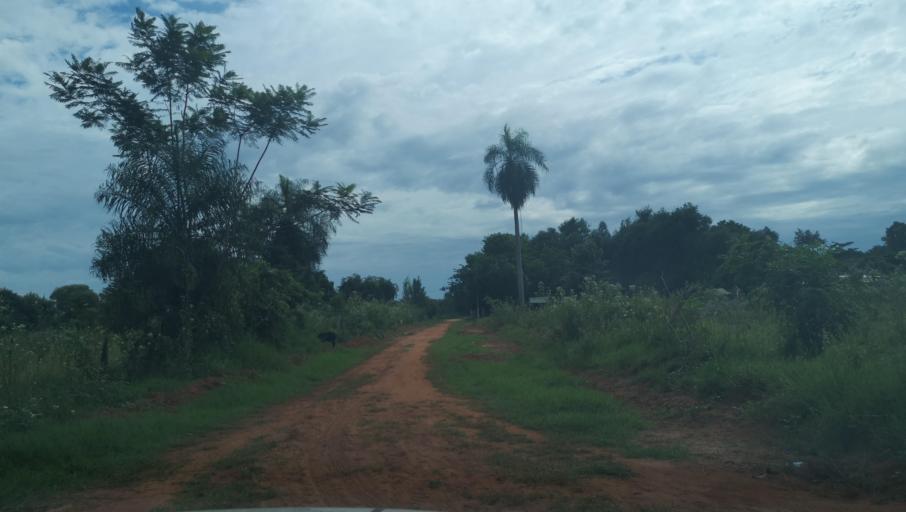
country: PY
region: San Pedro
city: Capiibary
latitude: -24.7224
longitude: -56.0200
